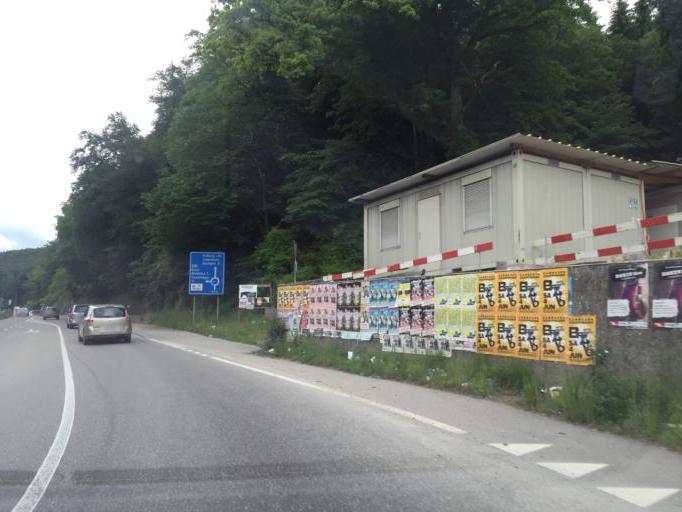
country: CH
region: Schaffhausen
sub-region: Bezirk Schaffhausen
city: Neuhausen
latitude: 47.6918
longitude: 8.6082
